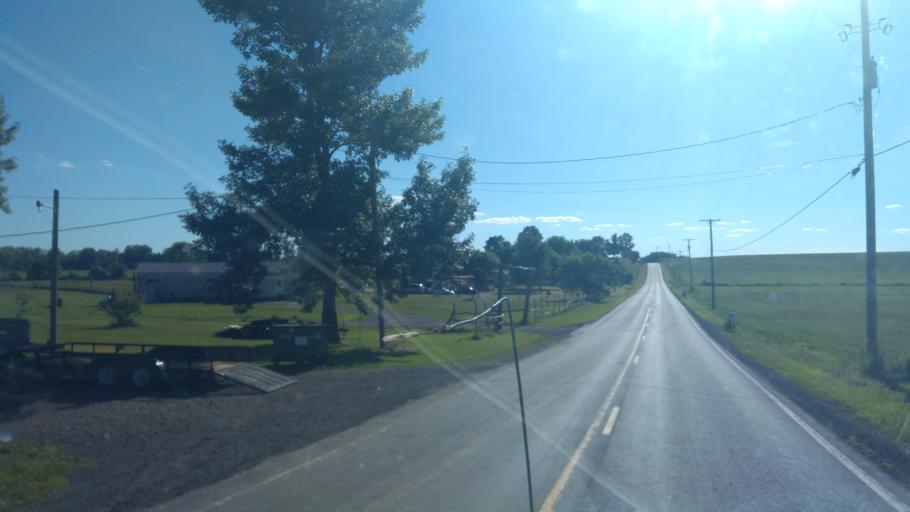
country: US
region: New York
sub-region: Wayne County
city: Clyde
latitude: 42.9966
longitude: -76.9096
